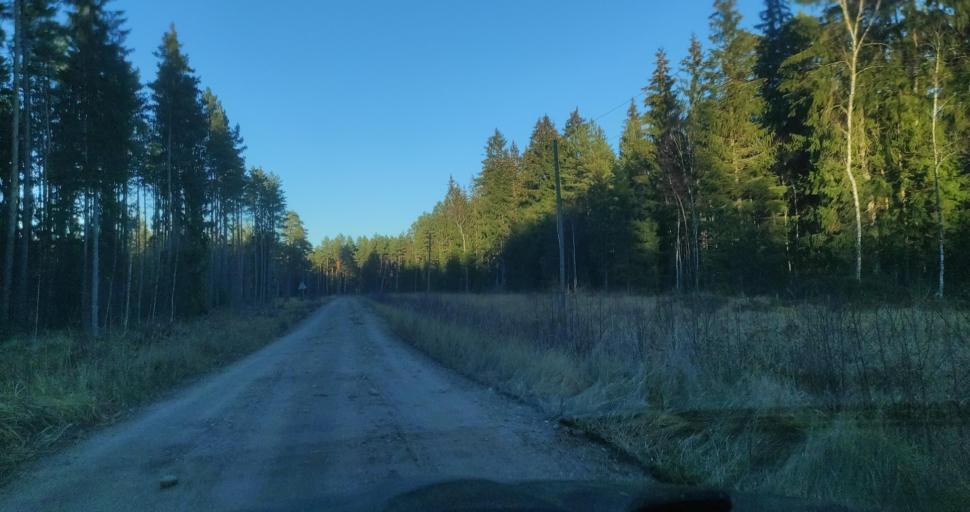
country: LV
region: Dundaga
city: Dundaga
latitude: 57.3768
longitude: 22.0804
